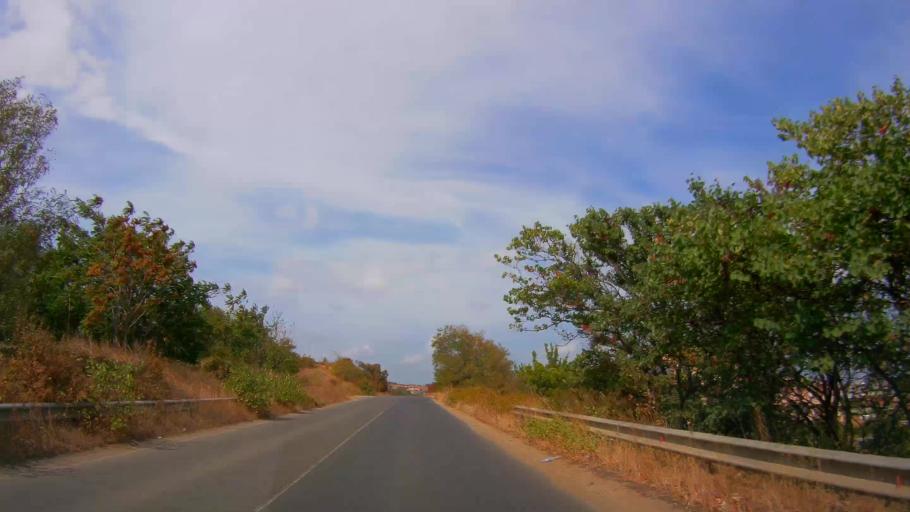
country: BG
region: Burgas
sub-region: Obshtina Sozopol
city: Sozopol
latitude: 42.4068
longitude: 27.7032
